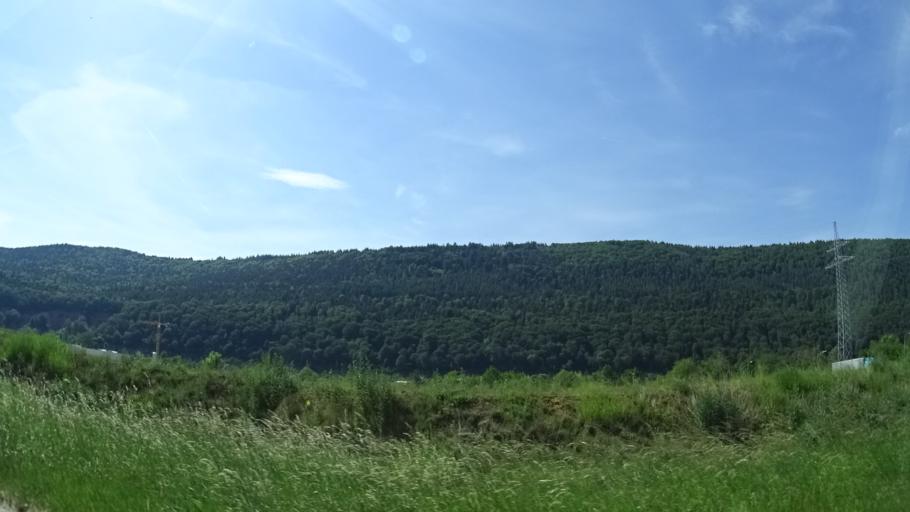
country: DE
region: Bavaria
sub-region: Regierungsbezirk Unterfranken
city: Burgstadt
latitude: 49.7315
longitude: 9.2786
